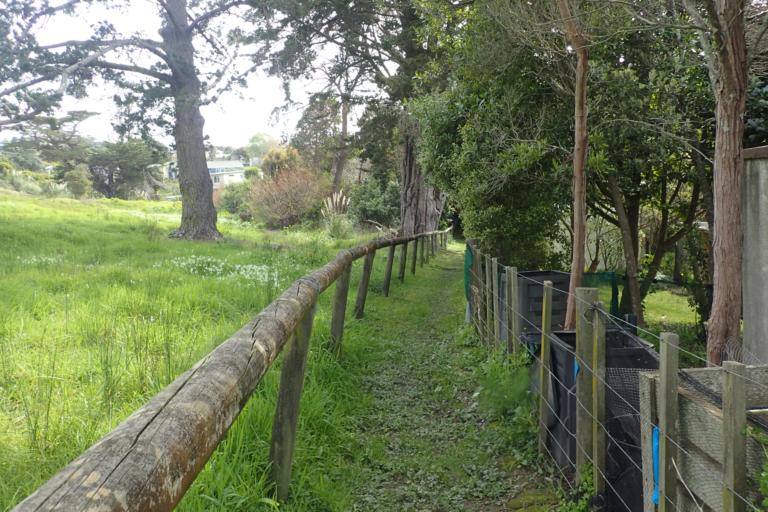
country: NZ
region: Auckland
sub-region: Auckland
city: Pakuranga
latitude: -36.7883
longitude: 175.0080
